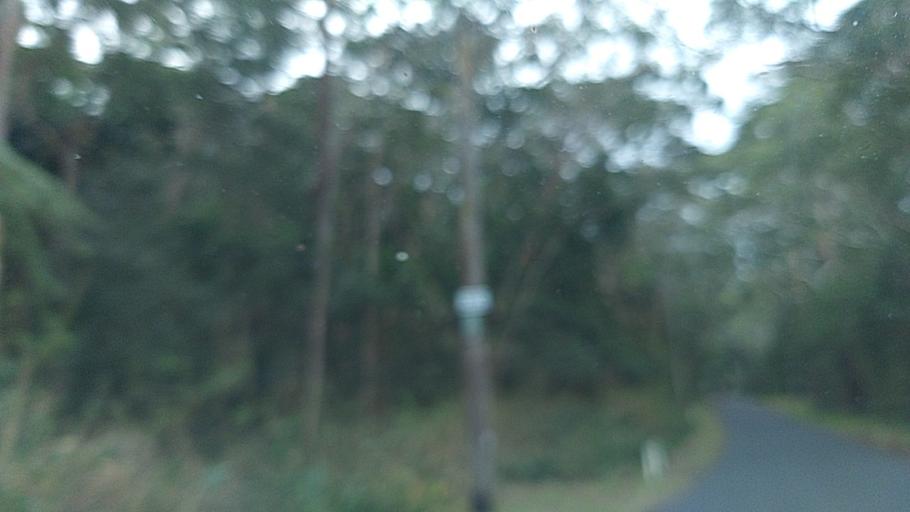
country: AU
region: New South Wales
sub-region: Wollongong
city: Bulli
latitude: -34.2987
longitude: 150.9308
